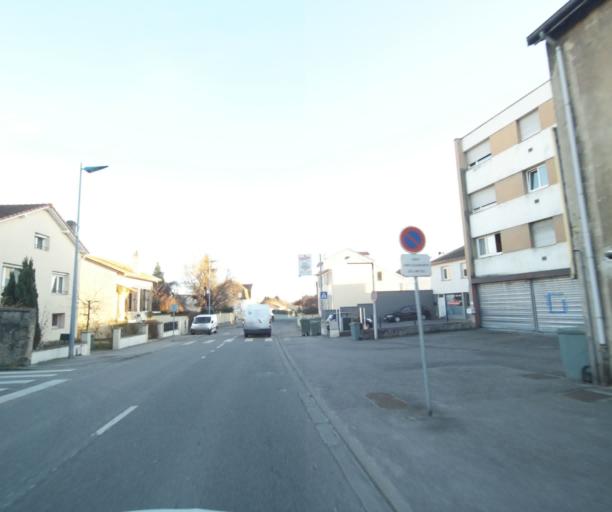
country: FR
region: Lorraine
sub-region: Departement de Meurthe-et-Moselle
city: Tomblaine
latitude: 48.6838
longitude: 6.2149
